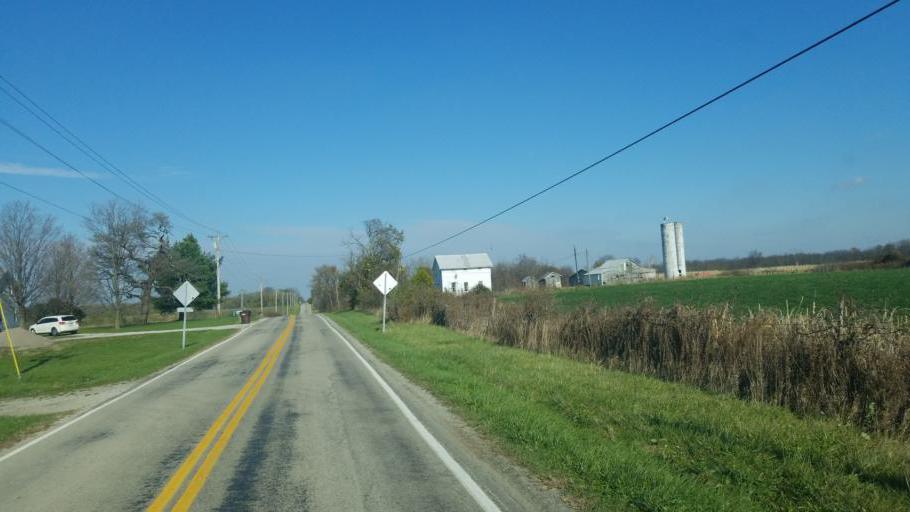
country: US
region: Ohio
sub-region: Lorain County
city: Wellington
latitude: 41.1505
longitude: -82.2691
